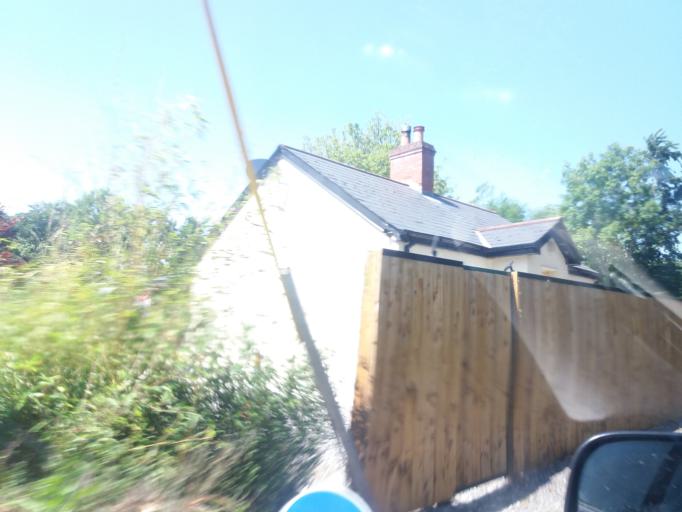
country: IE
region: Leinster
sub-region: An Mhi
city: Ashbourne
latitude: 53.5312
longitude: -6.3236
